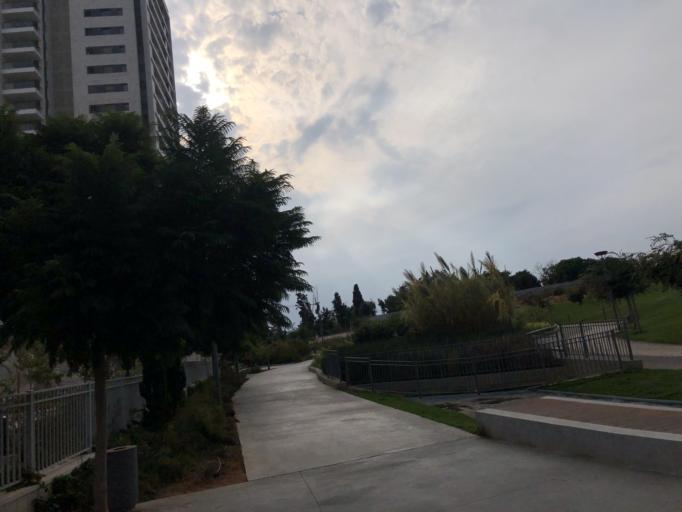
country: IL
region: Tel Aviv
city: Giv`at Shemu'el
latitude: 32.0549
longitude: 34.8454
